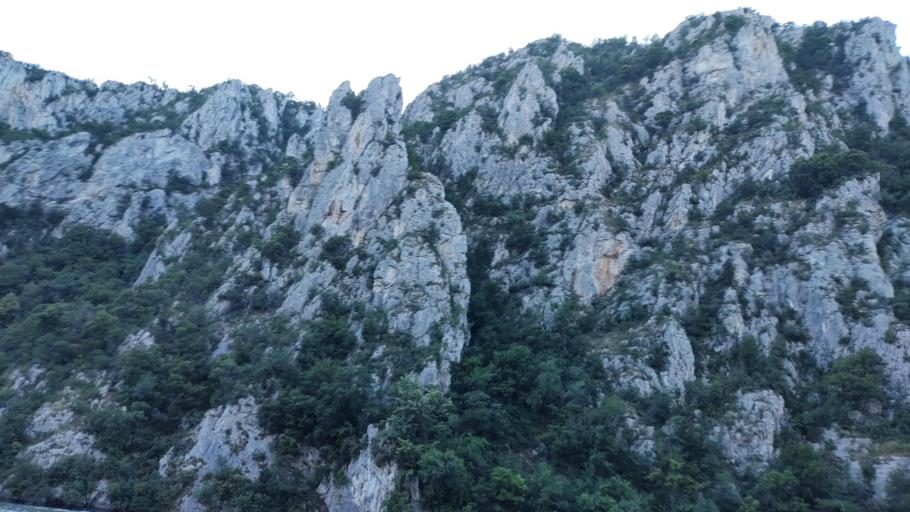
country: RO
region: Mehedinti
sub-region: Comuna Dubova
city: Dubova
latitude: 44.6127
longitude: 22.2717
